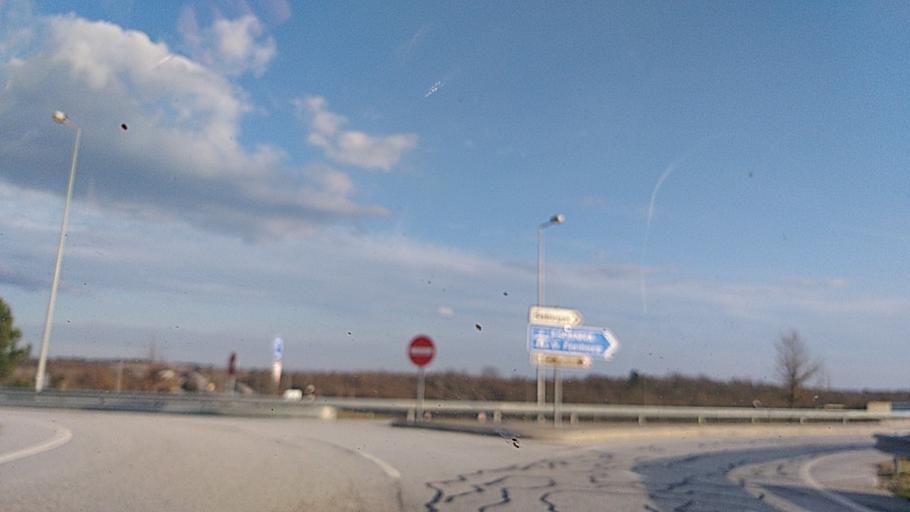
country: ES
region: Castille and Leon
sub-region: Provincia de Salamanca
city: Fuentes de Onoro
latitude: 40.6082
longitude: -6.9827
